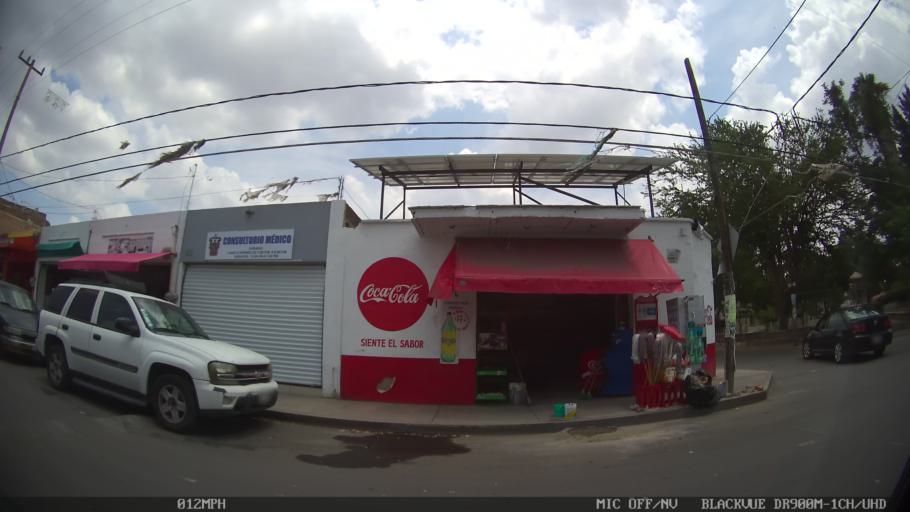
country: MX
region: Jalisco
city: Tonala
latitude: 20.6614
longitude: -103.2300
